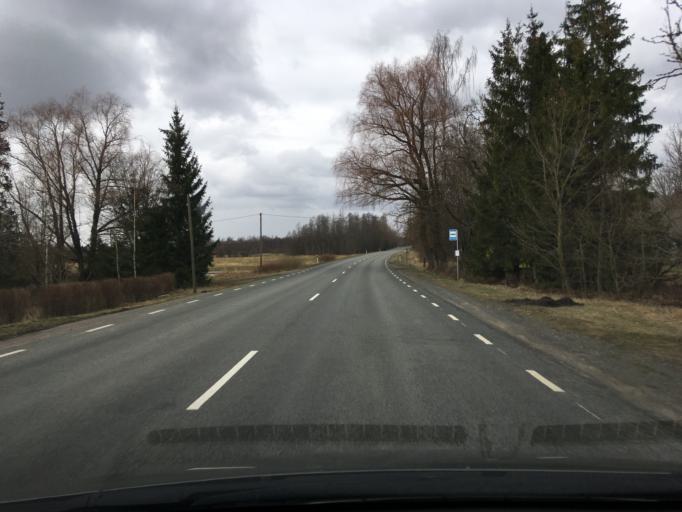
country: EE
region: Laeaene
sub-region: Lihula vald
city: Lihula
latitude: 58.5819
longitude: 23.9766
